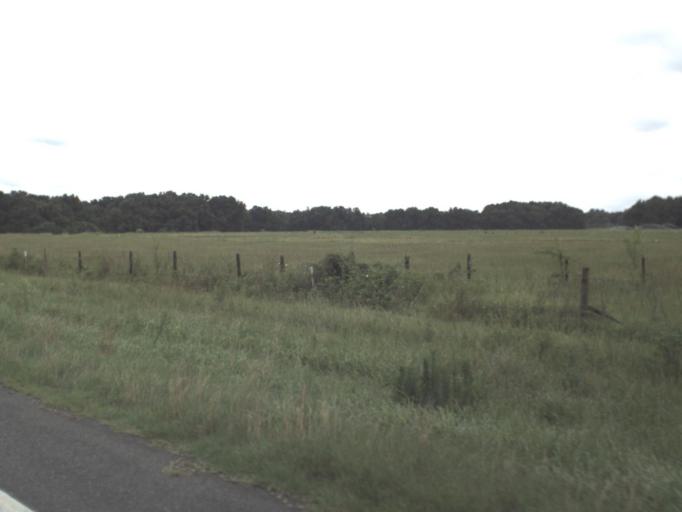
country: US
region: Florida
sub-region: Levy County
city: Williston
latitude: 29.3500
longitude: -82.4558
